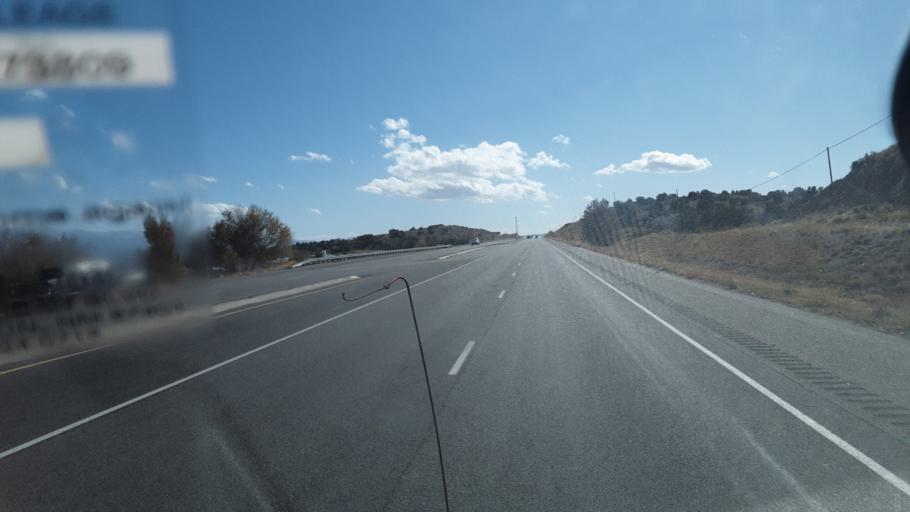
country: US
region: New Mexico
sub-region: Rio Arriba County
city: Ohkay Owingeh
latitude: 36.0309
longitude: -106.0938
